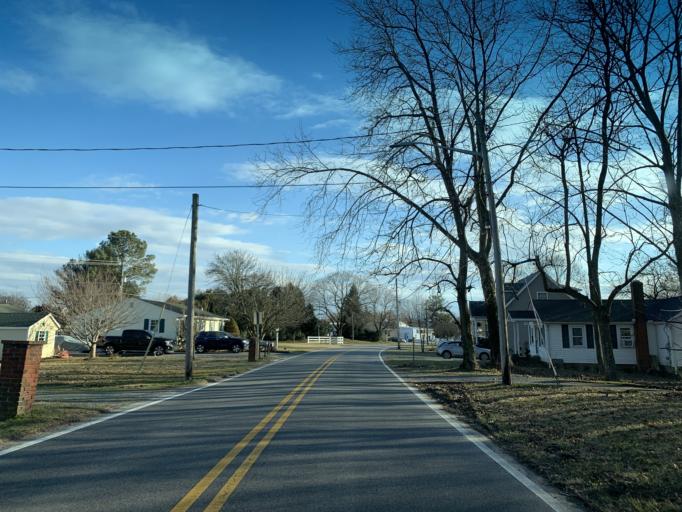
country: US
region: Maryland
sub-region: Queen Anne's County
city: Kingstown
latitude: 39.1502
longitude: -75.9786
